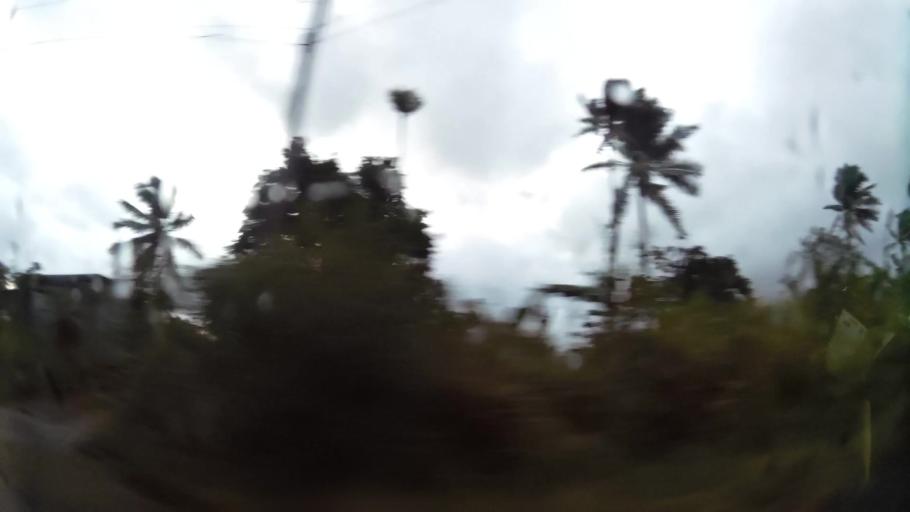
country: DM
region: Saint Andrew
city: Wesley
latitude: 15.5741
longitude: -61.3093
